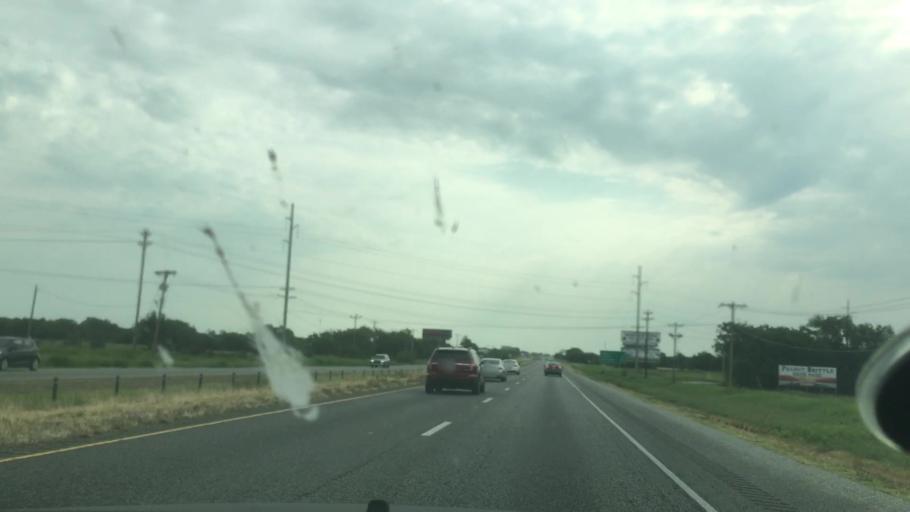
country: US
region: Oklahoma
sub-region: Bryan County
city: Colbert
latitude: 33.8808
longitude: -96.4962
